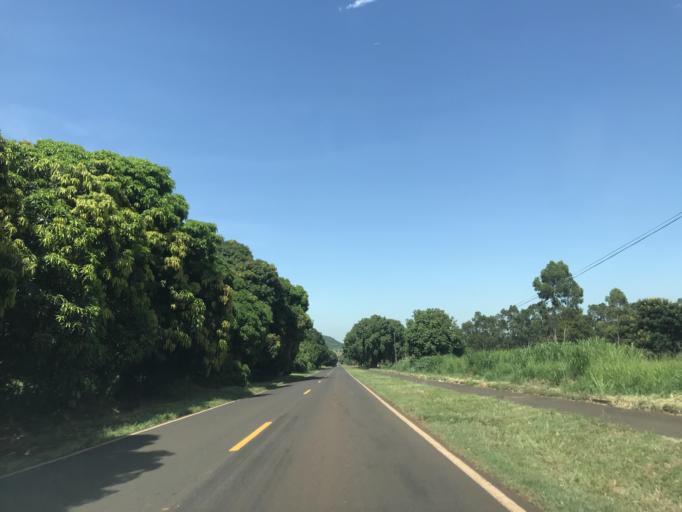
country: BR
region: Parana
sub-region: Terra Rica
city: Terra Rica
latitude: -22.7577
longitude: -52.6312
